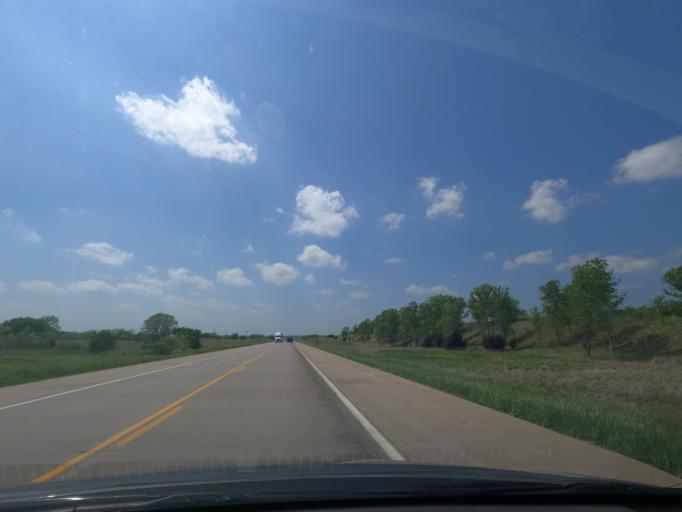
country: US
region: Kansas
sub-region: Wilson County
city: Fredonia
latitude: 37.6244
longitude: -96.0585
